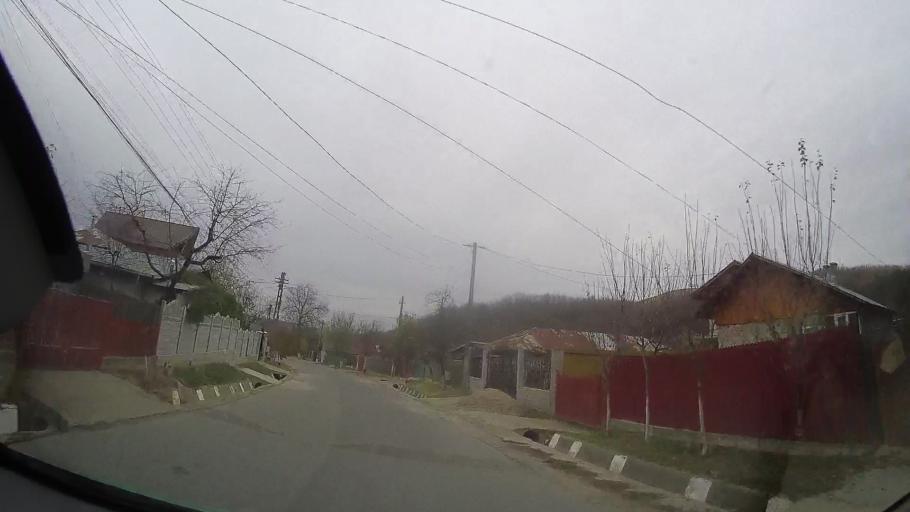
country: RO
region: Prahova
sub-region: Comuna Gornet-Cricov
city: Gornet-Cricov
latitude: 45.0575
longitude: 26.2849
